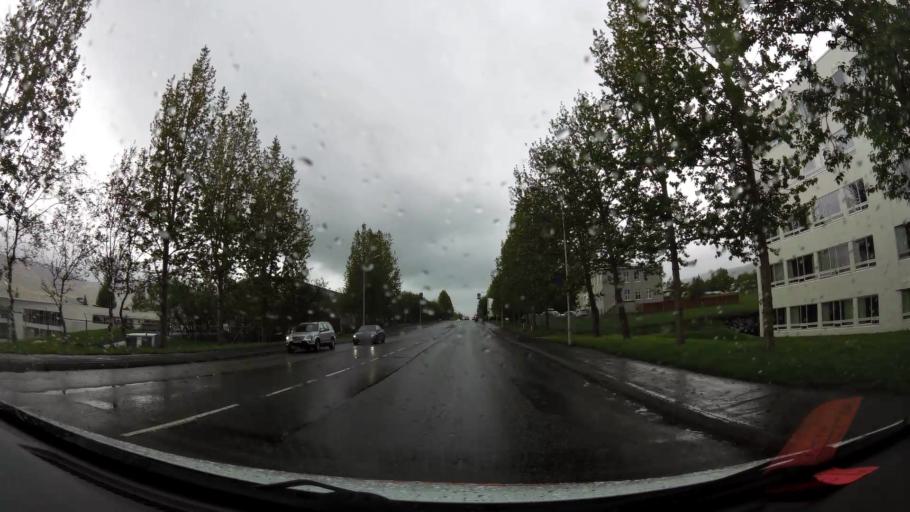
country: IS
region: Northeast
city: Akureyri
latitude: 65.6790
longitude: -18.0996
